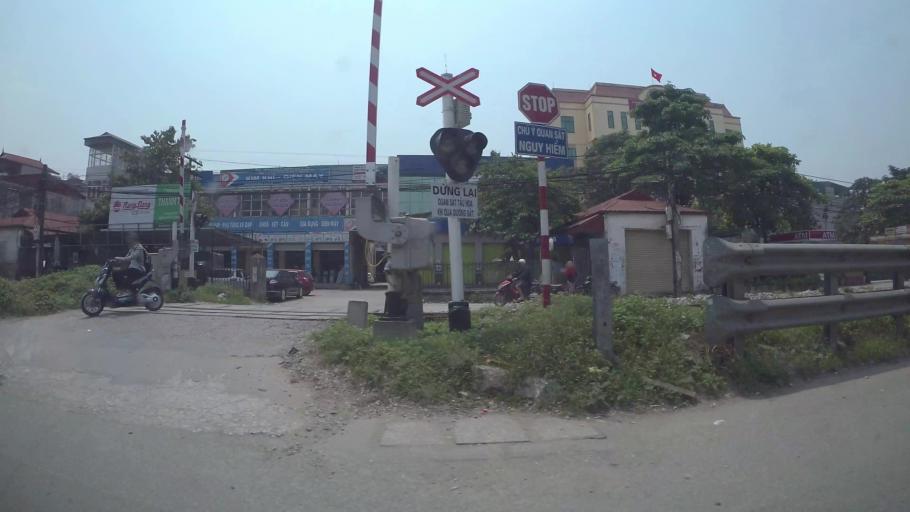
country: VN
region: Ha Noi
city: Van Dien
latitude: 20.9497
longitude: 105.8442
